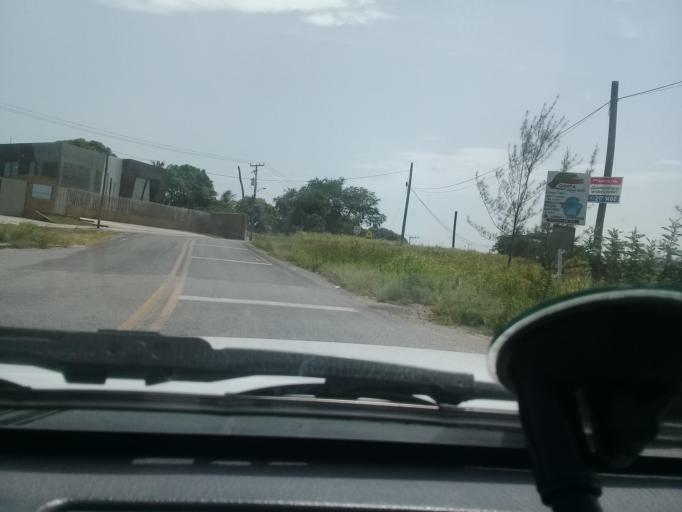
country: MX
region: Veracruz
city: Anahuac
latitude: 22.2127
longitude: -97.8286
